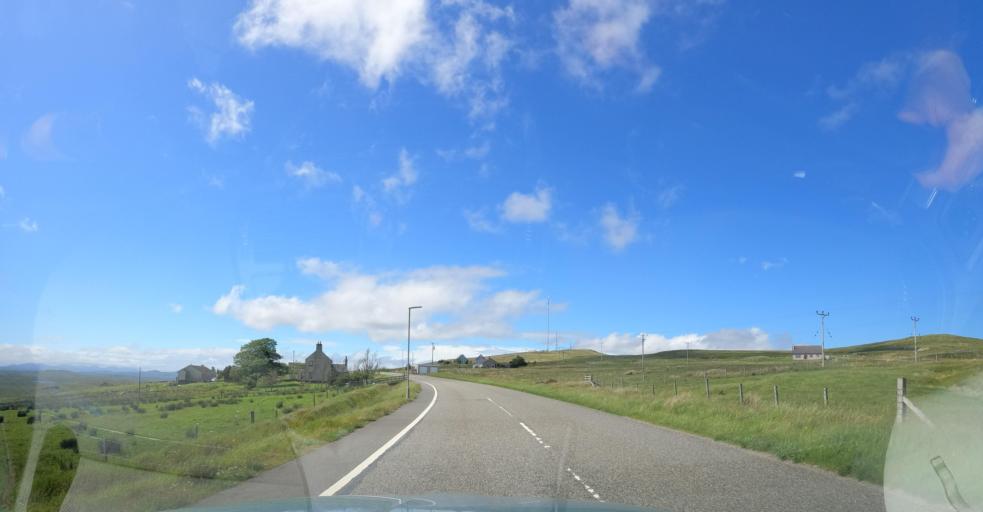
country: GB
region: Scotland
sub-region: Eilean Siar
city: Stornoway
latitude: 58.1708
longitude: -6.5697
